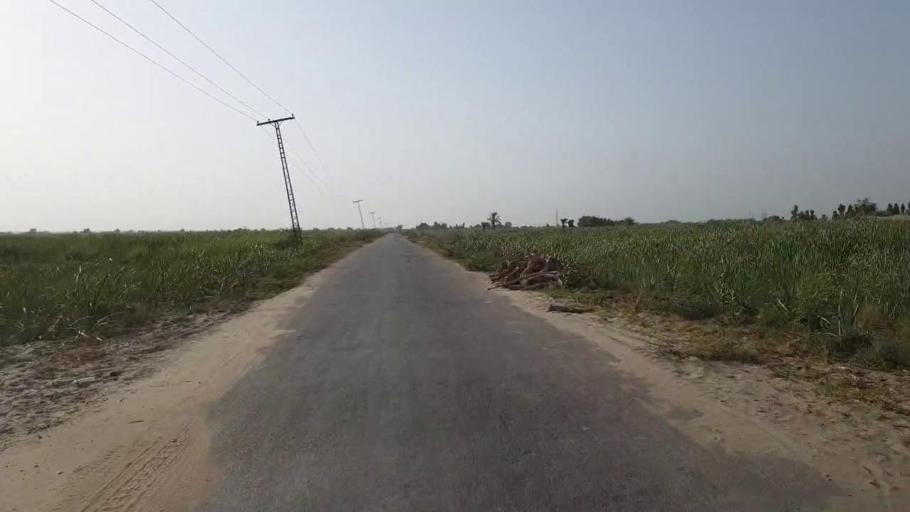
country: PK
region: Sindh
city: Jam Sahib
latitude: 26.4132
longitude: 68.8736
